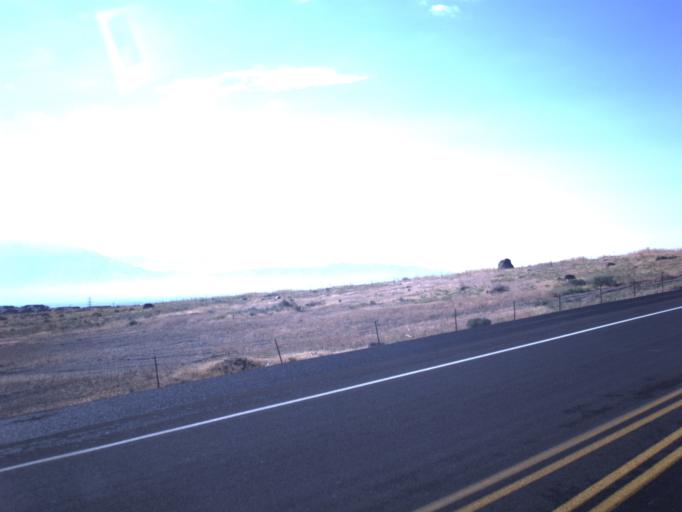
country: US
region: Utah
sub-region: Salt Lake County
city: Oquirrh
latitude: 40.6286
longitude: -112.0527
